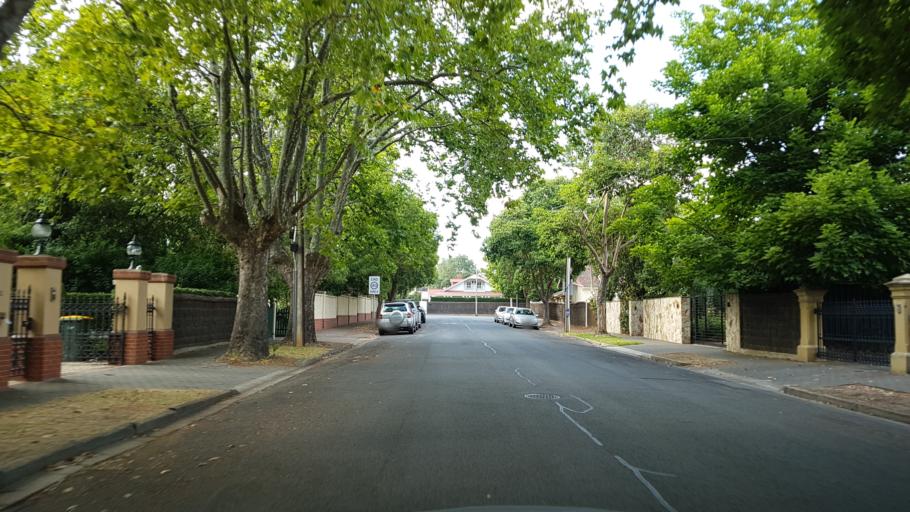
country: AU
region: South Australia
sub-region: Unley
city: Unley Park
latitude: -34.9650
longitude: 138.6003
